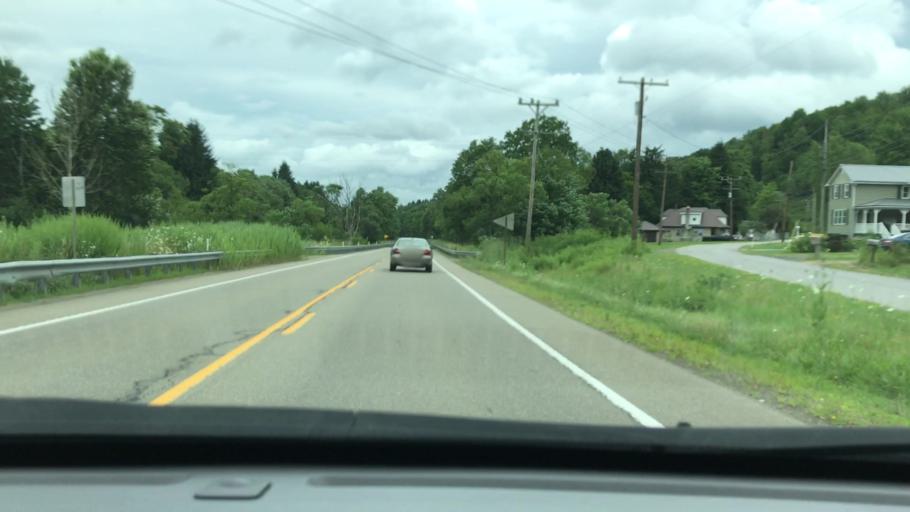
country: US
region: Pennsylvania
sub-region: Elk County
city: Johnsonburg
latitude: 41.5076
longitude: -78.6793
